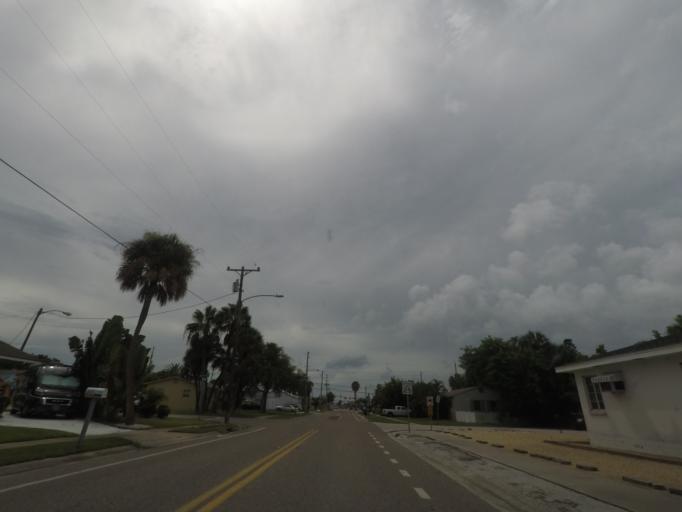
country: US
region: Florida
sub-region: Pinellas County
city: South Pasadena
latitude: 27.7438
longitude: -82.7528
